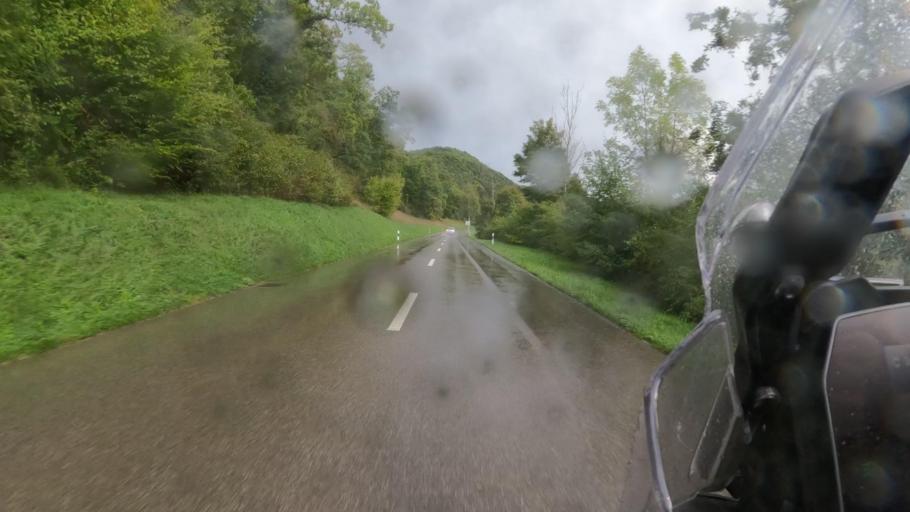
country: DE
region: Baden-Wuerttemberg
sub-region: Freiburg Region
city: Dettighofen
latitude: 47.6496
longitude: 8.5077
